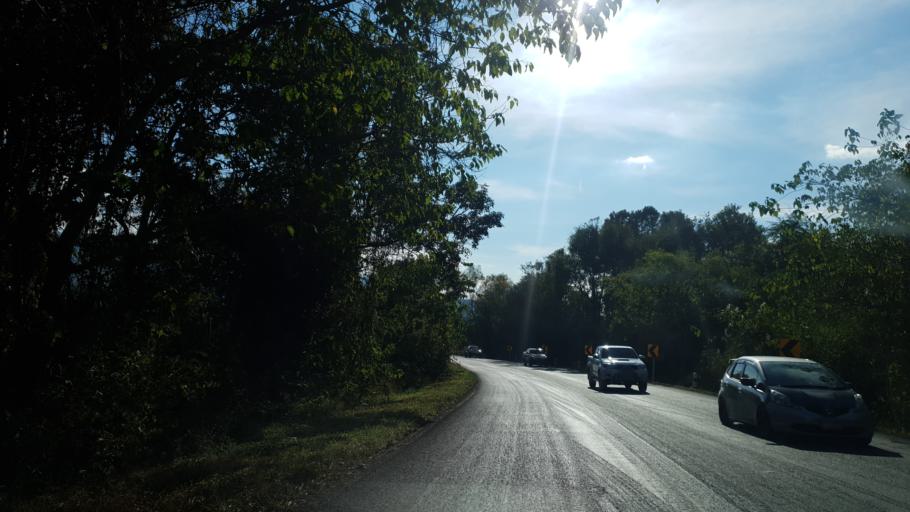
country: TH
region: Loei
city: Phu Ruea
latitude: 17.4470
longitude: 101.4769
